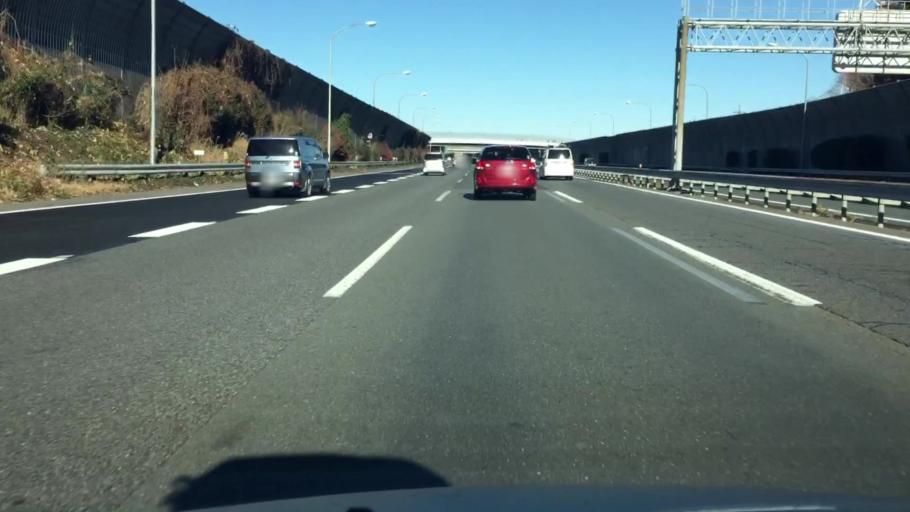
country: JP
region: Saitama
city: Sakado
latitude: 35.9361
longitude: 139.4054
